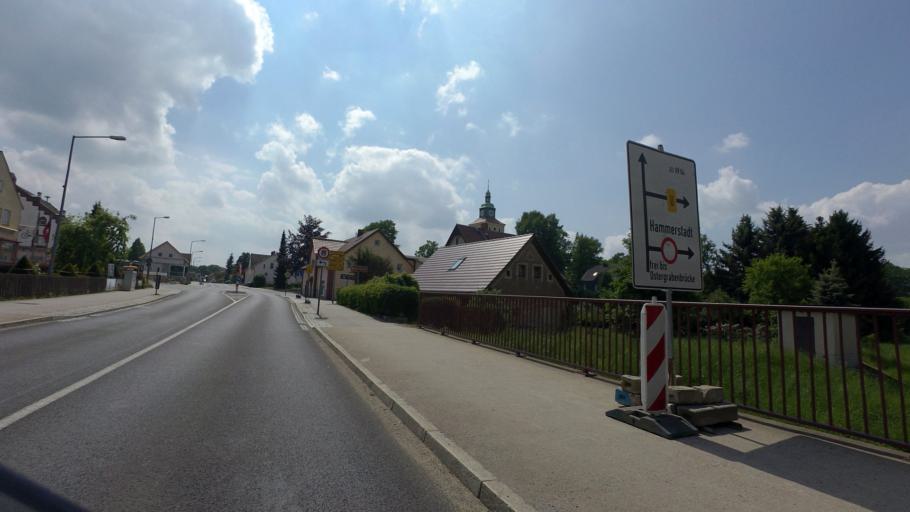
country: DE
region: Saxony
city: Rietschen
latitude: 51.3970
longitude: 14.7866
